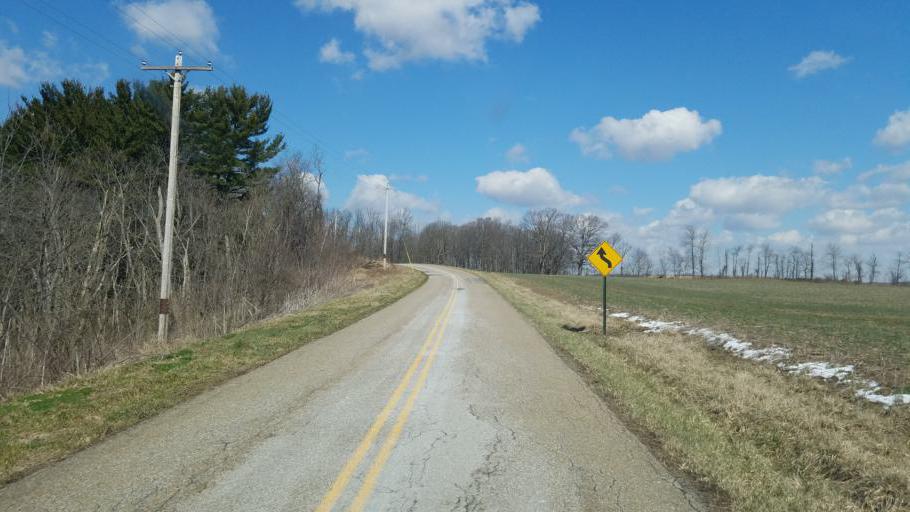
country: US
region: Ohio
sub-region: Licking County
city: Utica
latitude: 40.3066
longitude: -82.4870
